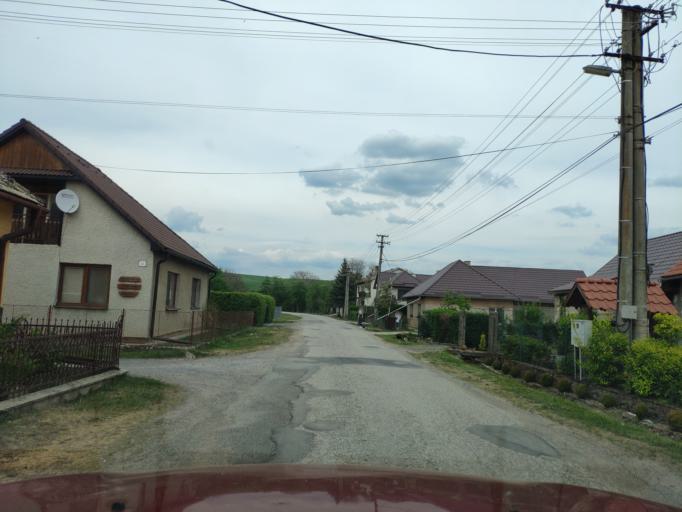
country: SK
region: Banskobystricky
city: Rimavska Sobota
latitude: 48.4822
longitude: 20.0729
